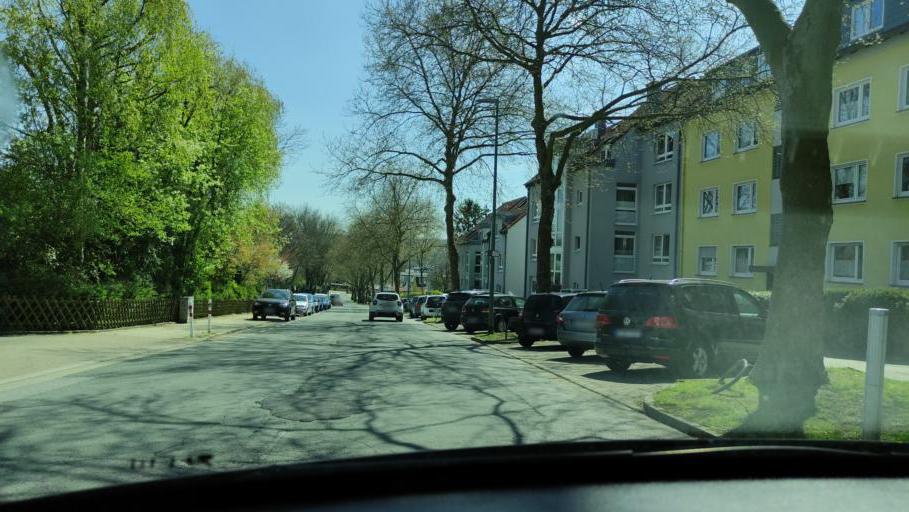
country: DE
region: North Rhine-Westphalia
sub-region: Regierungsbezirk Dusseldorf
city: Velbert
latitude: 51.3997
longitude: 7.0662
